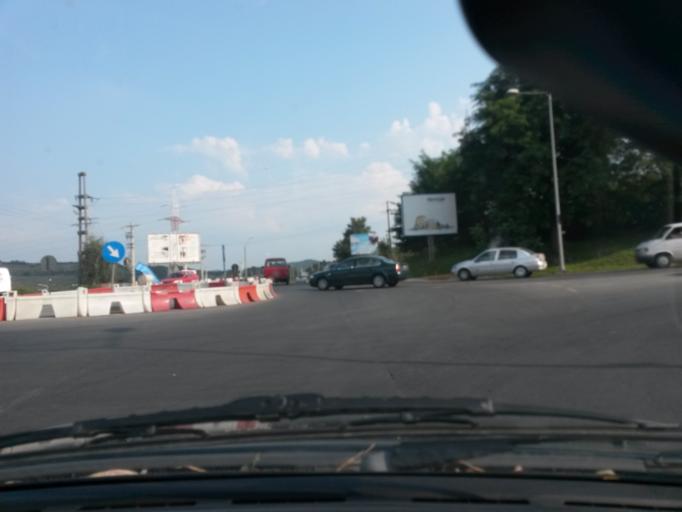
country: RO
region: Mures
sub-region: Comuna Corunca
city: Corunca
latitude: 46.5312
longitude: 24.5940
